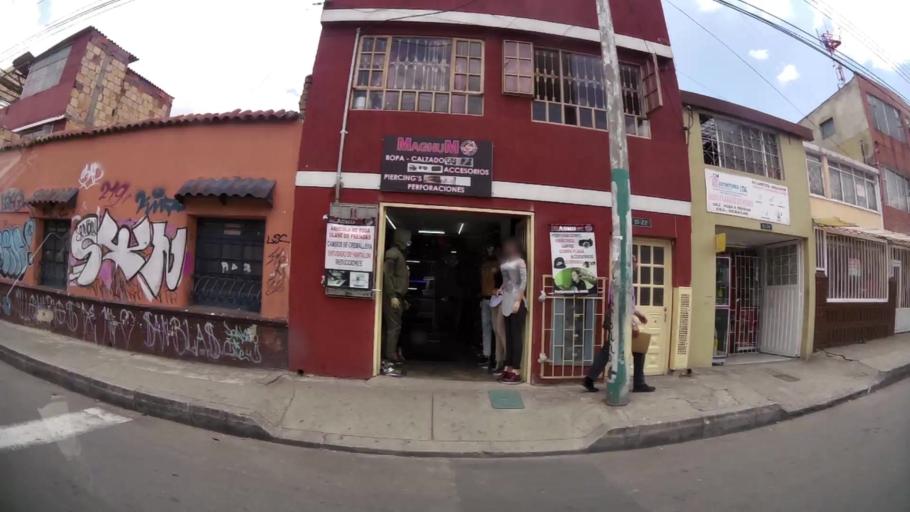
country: CO
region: Bogota D.C.
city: Bogota
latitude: 4.5767
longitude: -74.0885
